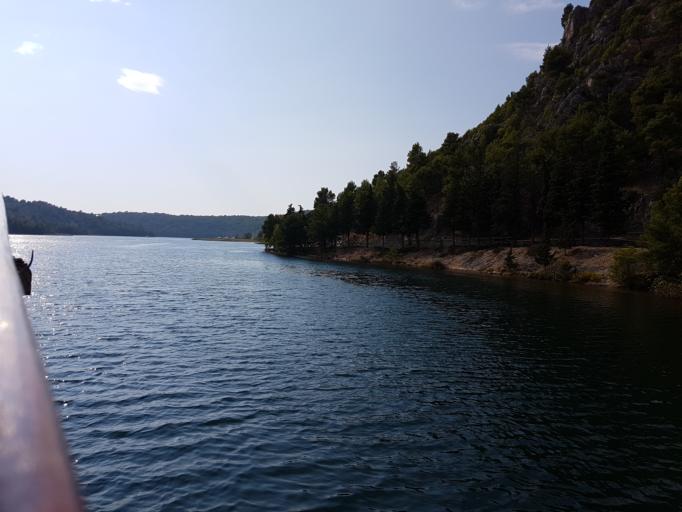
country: HR
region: Sibensko-Kniniska
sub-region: Grad Sibenik
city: Sibenik
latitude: 43.8186
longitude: 15.9346
